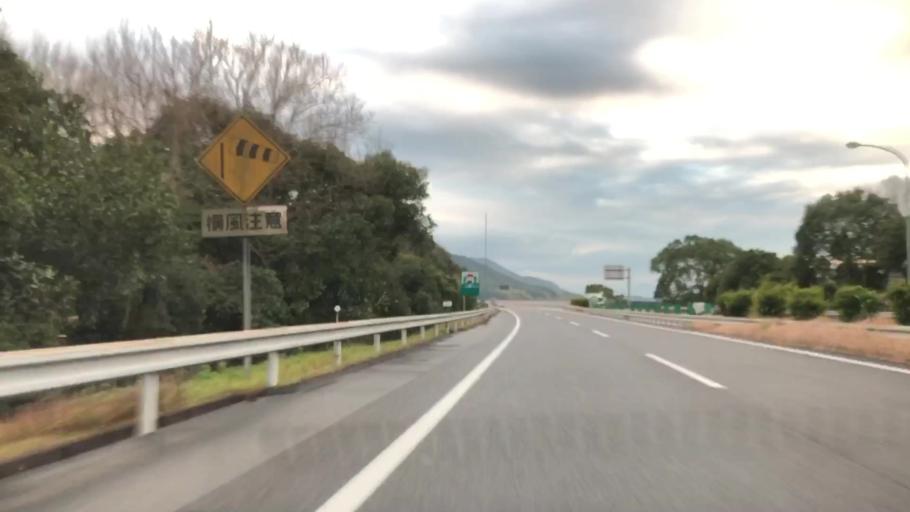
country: JP
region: Saga Prefecture
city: Takeocho-takeo
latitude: 33.2170
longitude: 130.0504
